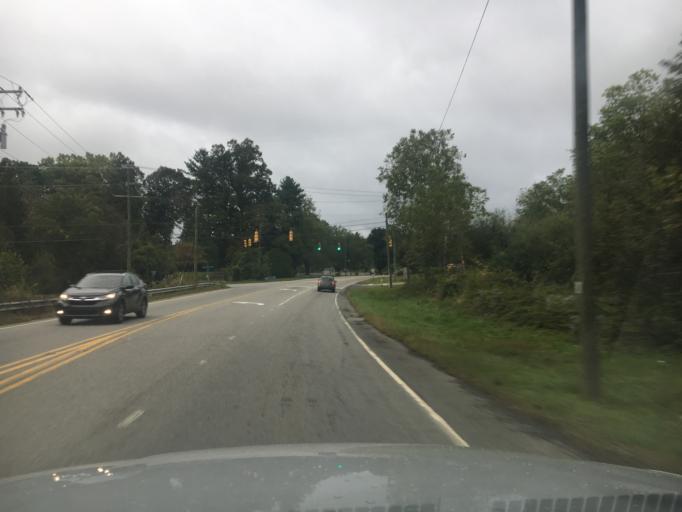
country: US
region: North Carolina
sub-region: Henderson County
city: Horse Shoe
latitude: 35.3427
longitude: -82.5578
